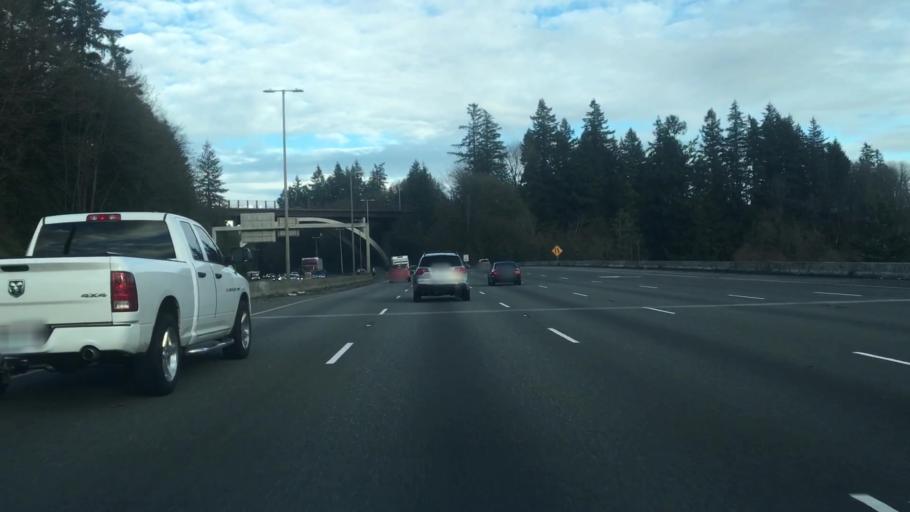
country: US
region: Washington
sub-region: Thurston County
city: Olympia
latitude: 47.0240
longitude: -122.9020
